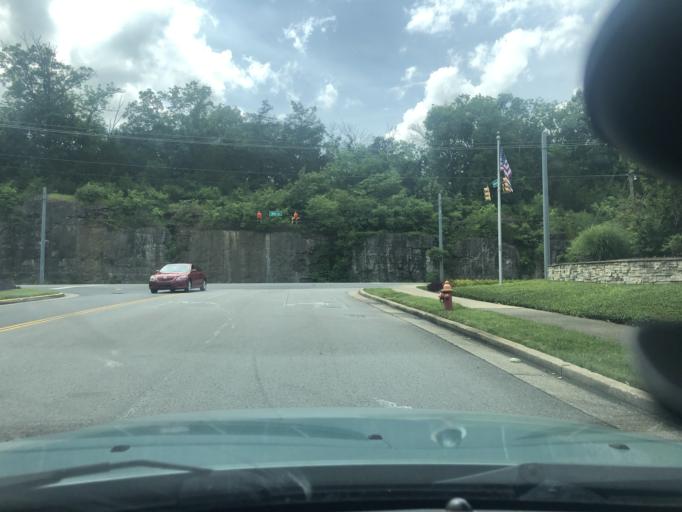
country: US
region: Tennessee
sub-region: Rutherford County
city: La Vergne
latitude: 36.1227
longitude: -86.6300
